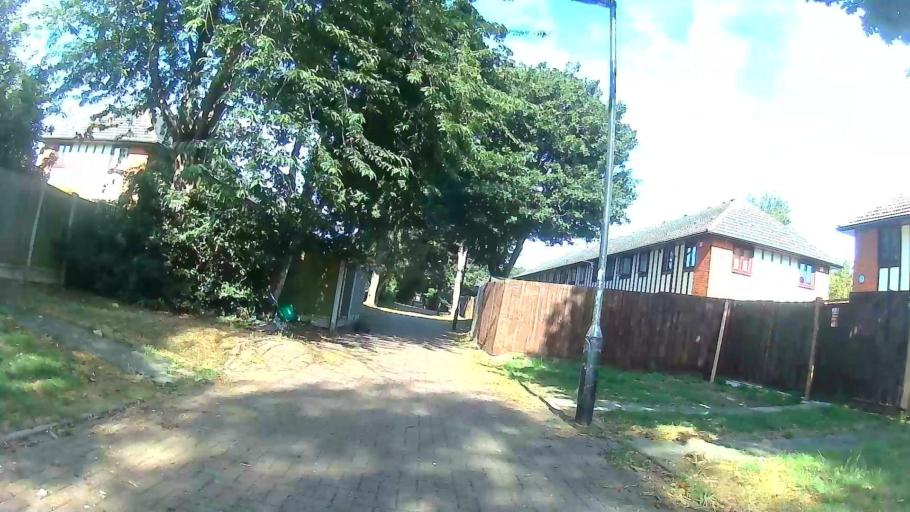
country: GB
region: England
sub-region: Greater London
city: Woolwich
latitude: 51.5099
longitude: 0.0658
